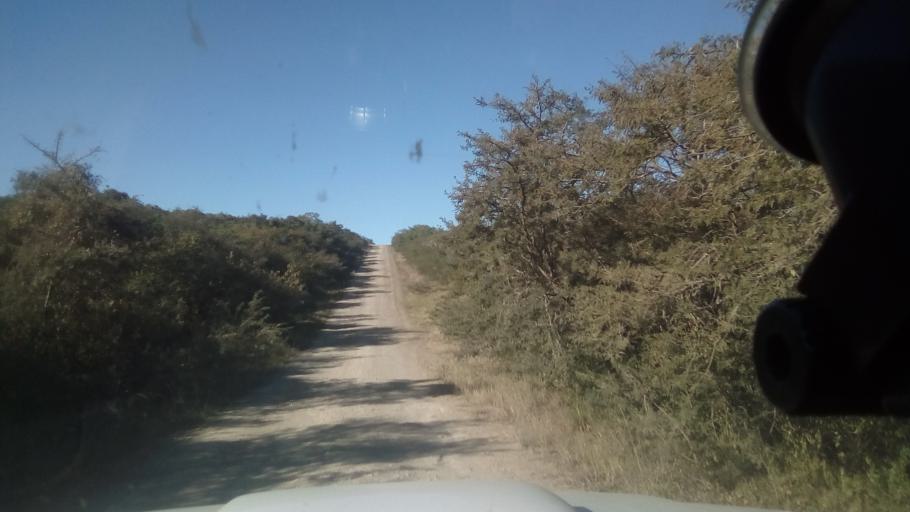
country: ZA
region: Eastern Cape
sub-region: Buffalo City Metropolitan Municipality
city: Bhisho
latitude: -32.7528
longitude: 27.3421
